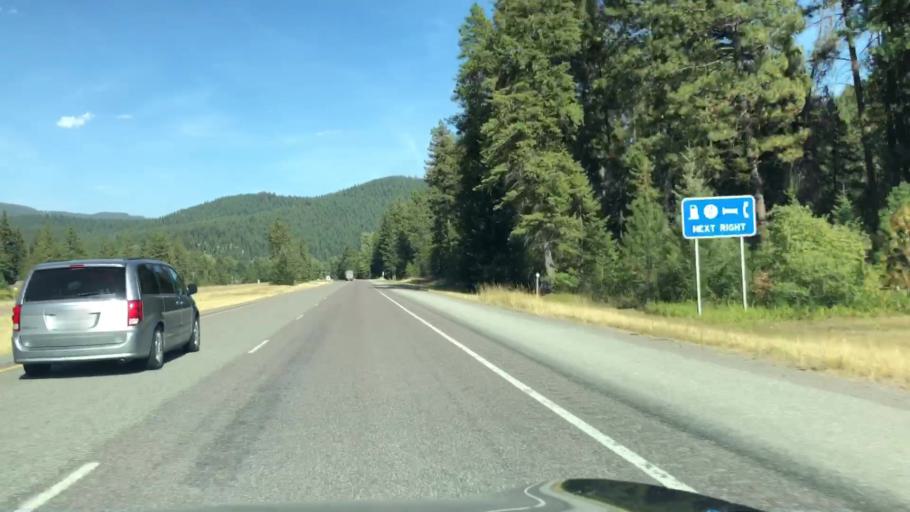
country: US
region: Montana
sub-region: Sanders County
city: Thompson Falls
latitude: 47.3765
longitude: -115.3710
